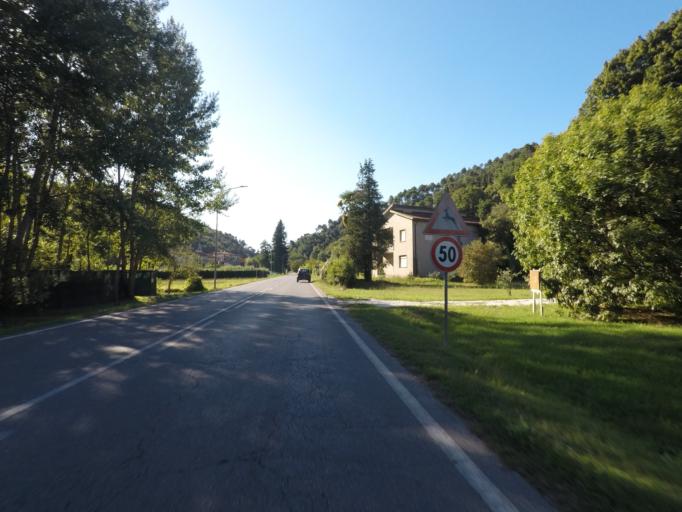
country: IT
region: Tuscany
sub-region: Provincia di Lucca
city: Massarosa
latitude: 43.9008
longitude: 10.3822
